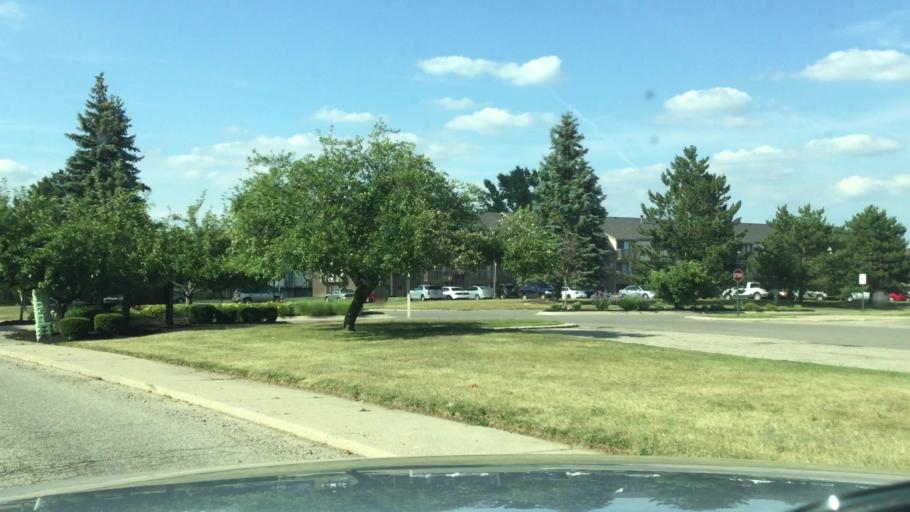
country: US
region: Michigan
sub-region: Genesee County
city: Grand Blanc
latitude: 42.9284
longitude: -83.5926
